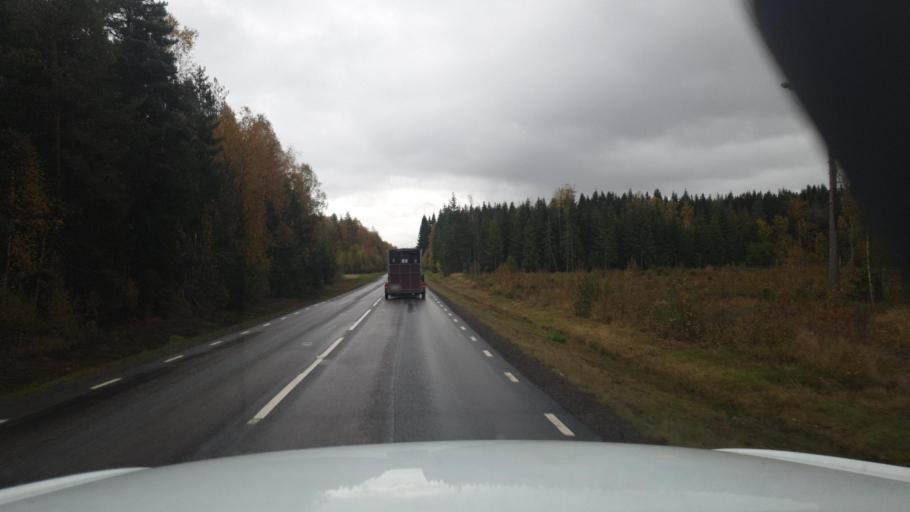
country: SE
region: Vaermland
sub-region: Eda Kommun
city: Charlottenberg
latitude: 59.8457
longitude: 12.2905
